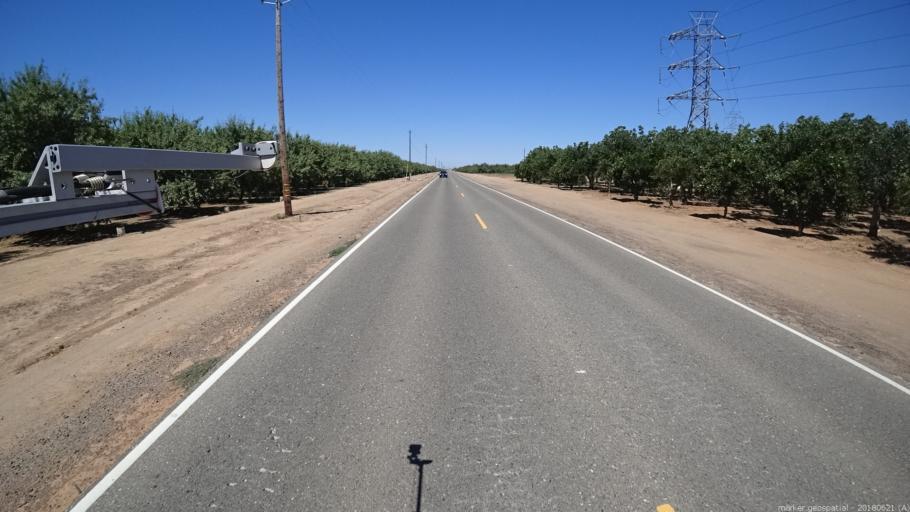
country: US
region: California
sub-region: Fresno County
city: Biola
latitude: 36.8515
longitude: -119.9194
